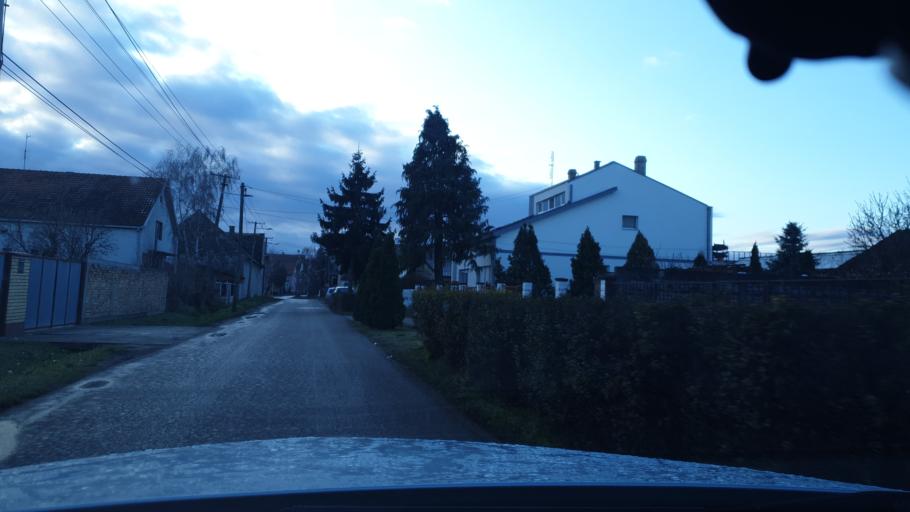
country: RS
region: Autonomna Pokrajina Vojvodina
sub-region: Sremski Okrug
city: Stara Pazova
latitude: 44.9864
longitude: 20.1657
